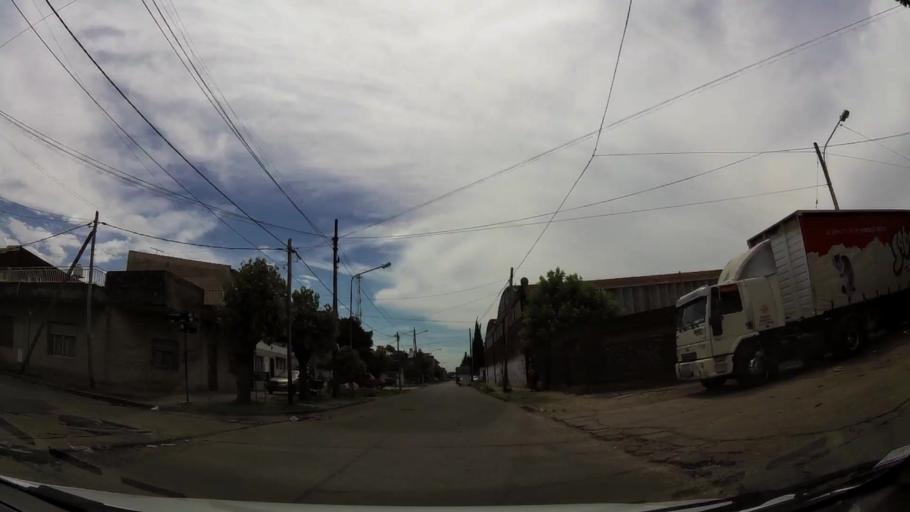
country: AR
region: Buenos Aires
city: San Justo
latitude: -34.6844
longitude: -58.5339
